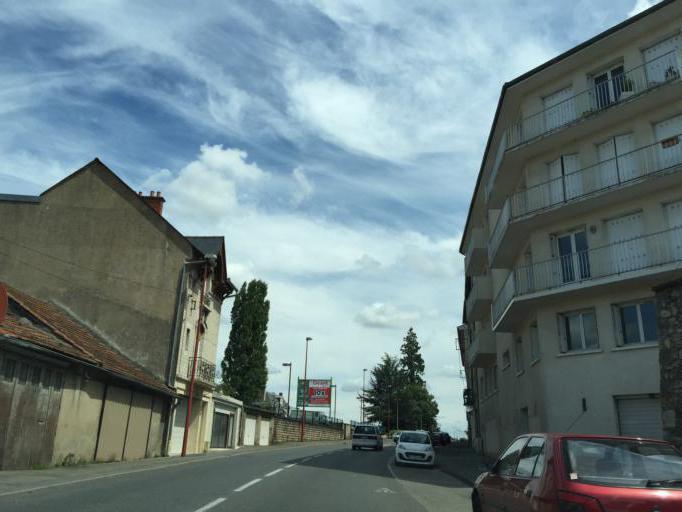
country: FR
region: Midi-Pyrenees
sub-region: Departement de l'Aveyron
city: Rodez
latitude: 44.3622
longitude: 2.5780
